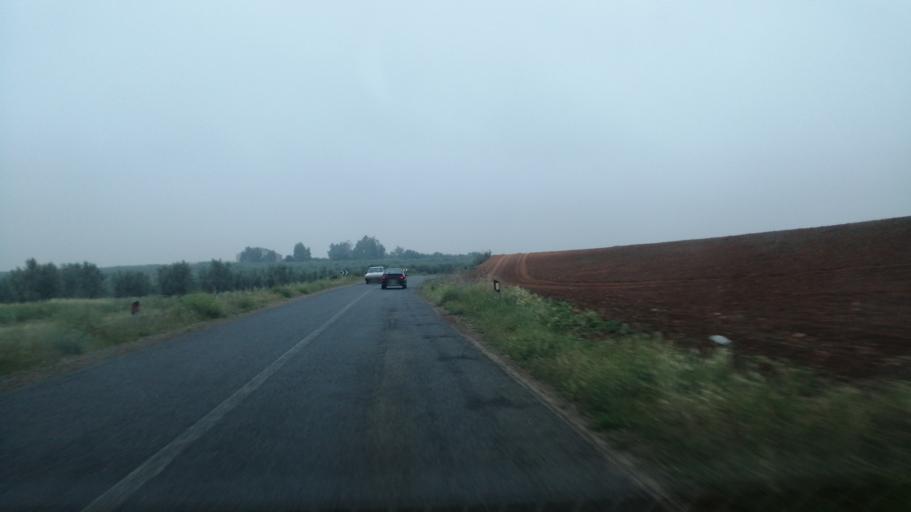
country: MA
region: Rabat-Sale-Zemmour-Zaer
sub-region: Khemisset
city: Tiflet
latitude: 33.7531
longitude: -6.2673
